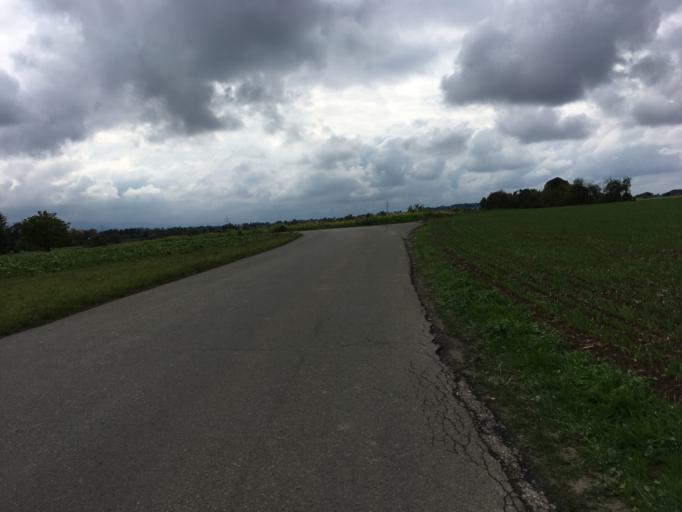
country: DE
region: Baden-Wuerttemberg
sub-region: Tuebingen Region
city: Kusterdingen
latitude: 48.5088
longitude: 9.1242
